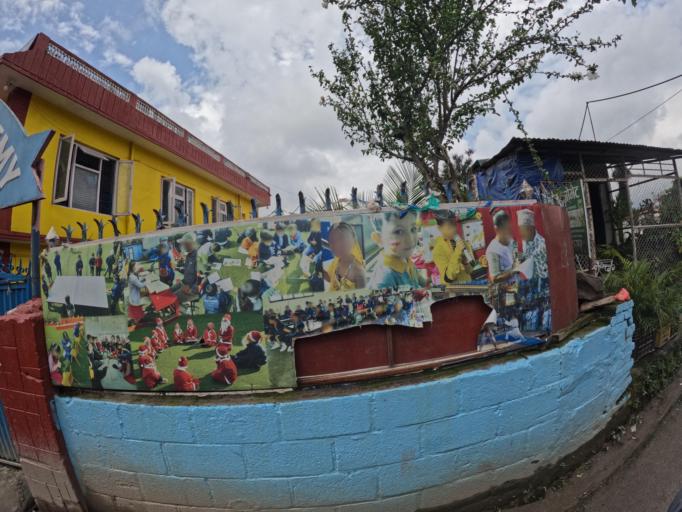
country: NP
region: Central Region
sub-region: Bagmati Zone
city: Kathmandu
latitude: 27.7511
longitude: 85.3177
